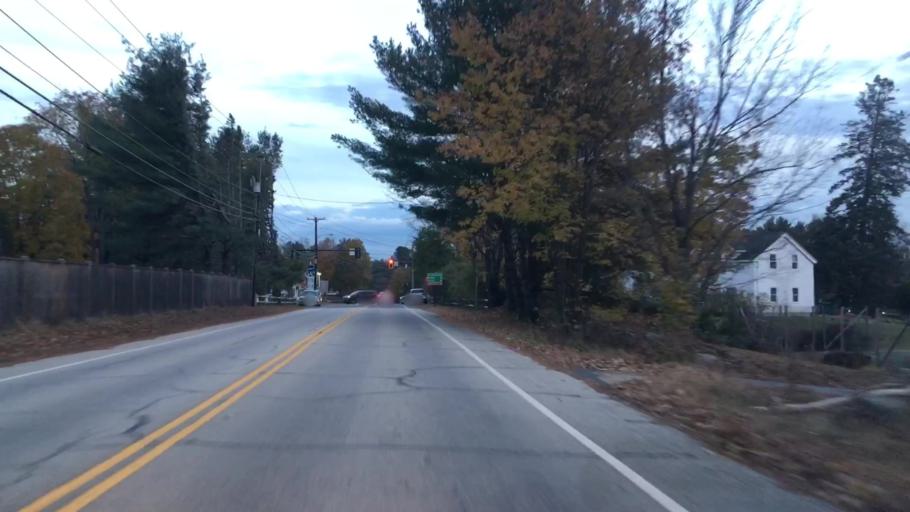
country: US
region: New Hampshire
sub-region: Hillsborough County
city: Milford
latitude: 42.8612
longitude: -71.6270
